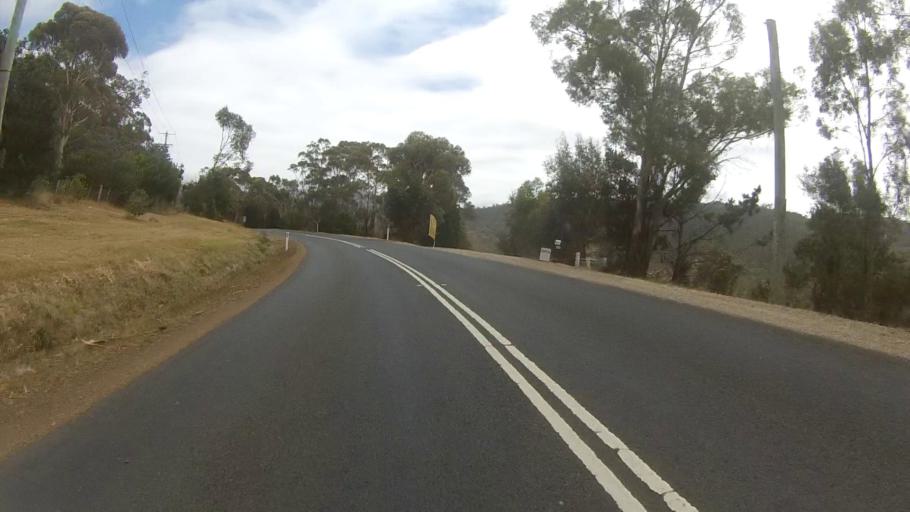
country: AU
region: Tasmania
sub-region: Kingborough
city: Margate
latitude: -43.0092
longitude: 147.2436
